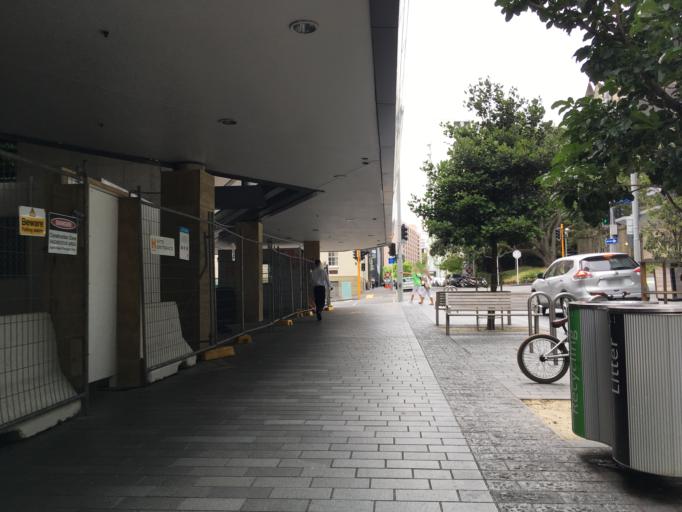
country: NZ
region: Auckland
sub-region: Auckland
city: Auckland
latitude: -36.8498
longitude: 174.7618
